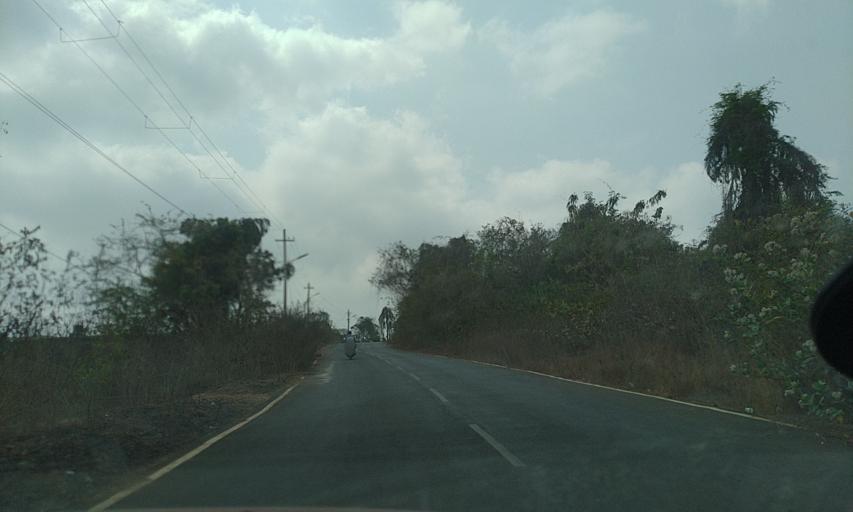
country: IN
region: Goa
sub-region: North Goa
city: Goa Velha
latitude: 15.4911
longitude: 73.9111
